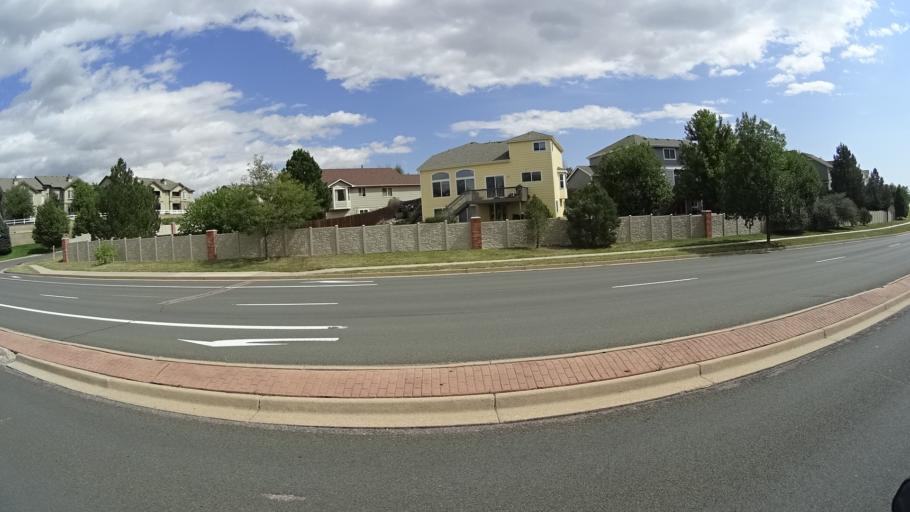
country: US
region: Colorado
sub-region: El Paso County
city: Cimarron Hills
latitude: 38.8952
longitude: -104.7019
